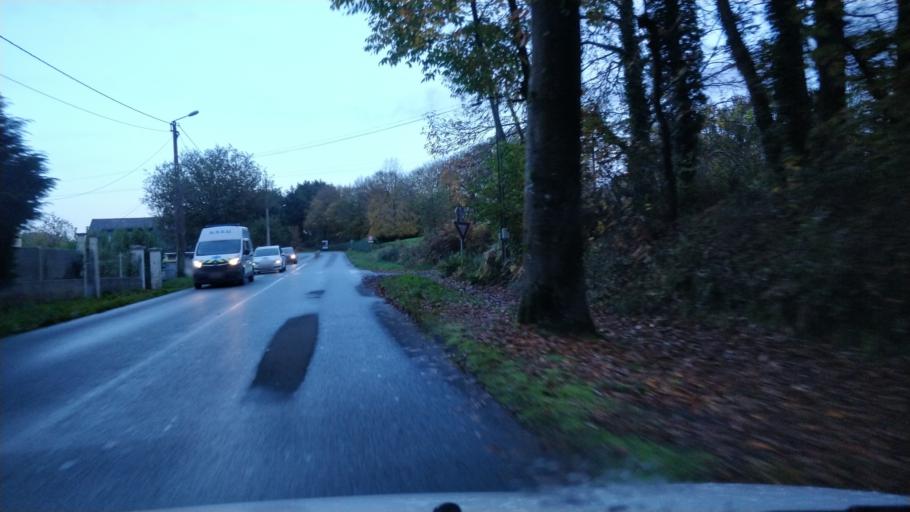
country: FR
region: Brittany
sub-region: Departement du Morbihan
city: Pontivy
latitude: 48.0784
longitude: -2.9540
